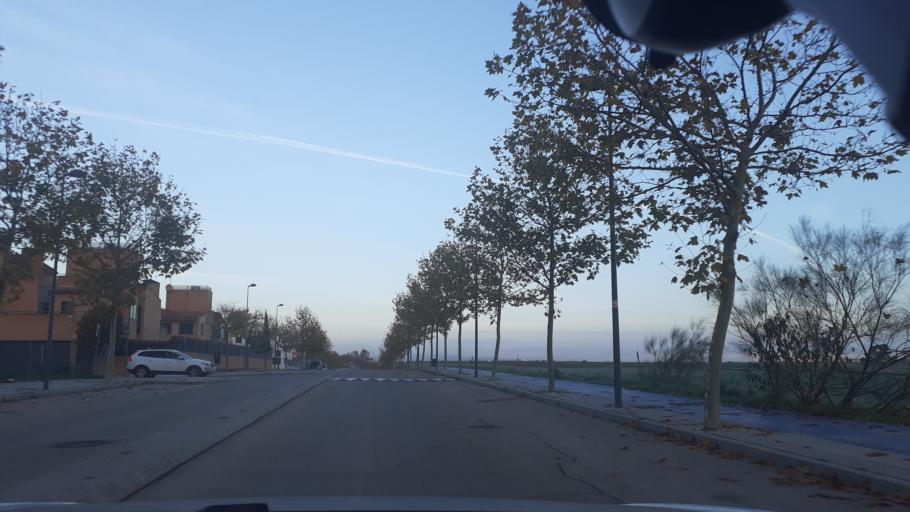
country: ES
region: Madrid
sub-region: Provincia de Madrid
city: Paracuellos de Jarama
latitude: 40.5062
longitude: -3.5087
